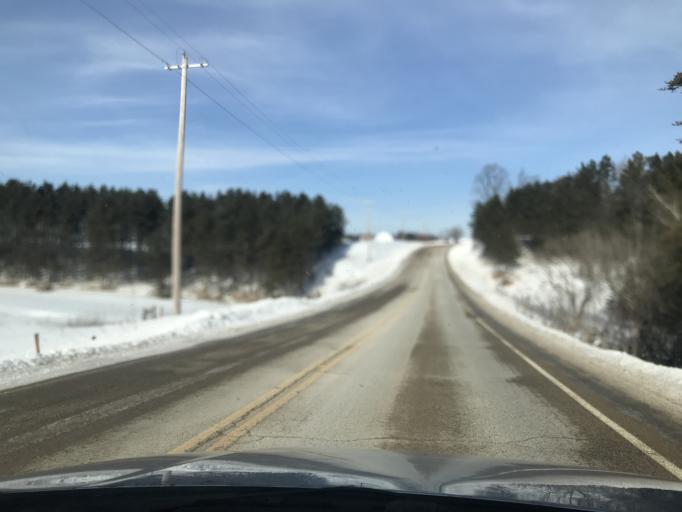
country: US
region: Wisconsin
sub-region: Oconto County
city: Oconto Falls
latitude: 45.1450
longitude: -88.1769
